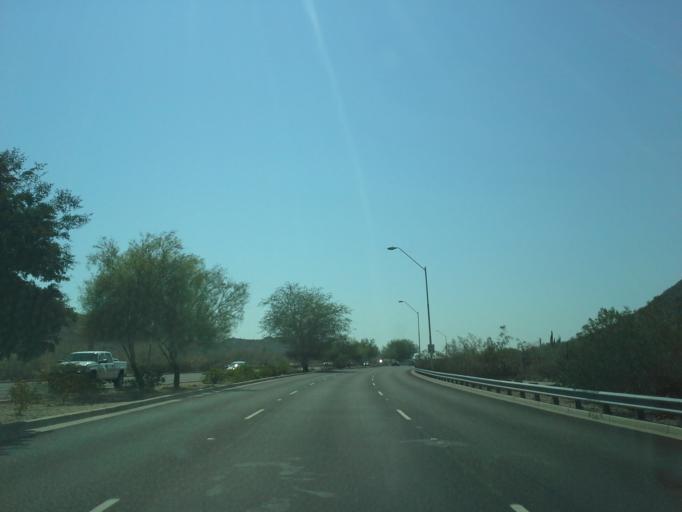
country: US
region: Arizona
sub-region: Maricopa County
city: Fountain Hills
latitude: 33.5817
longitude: -111.7819
